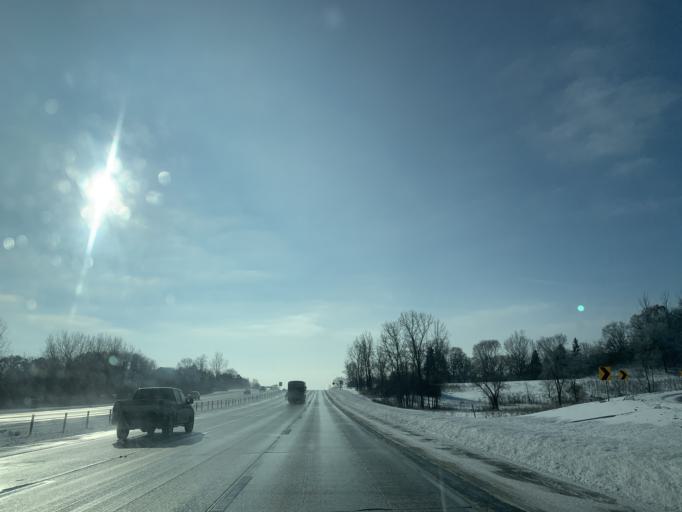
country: US
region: Minnesota
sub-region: Dakota County
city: Apple Valley
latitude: 44.7592
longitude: -93.2178
